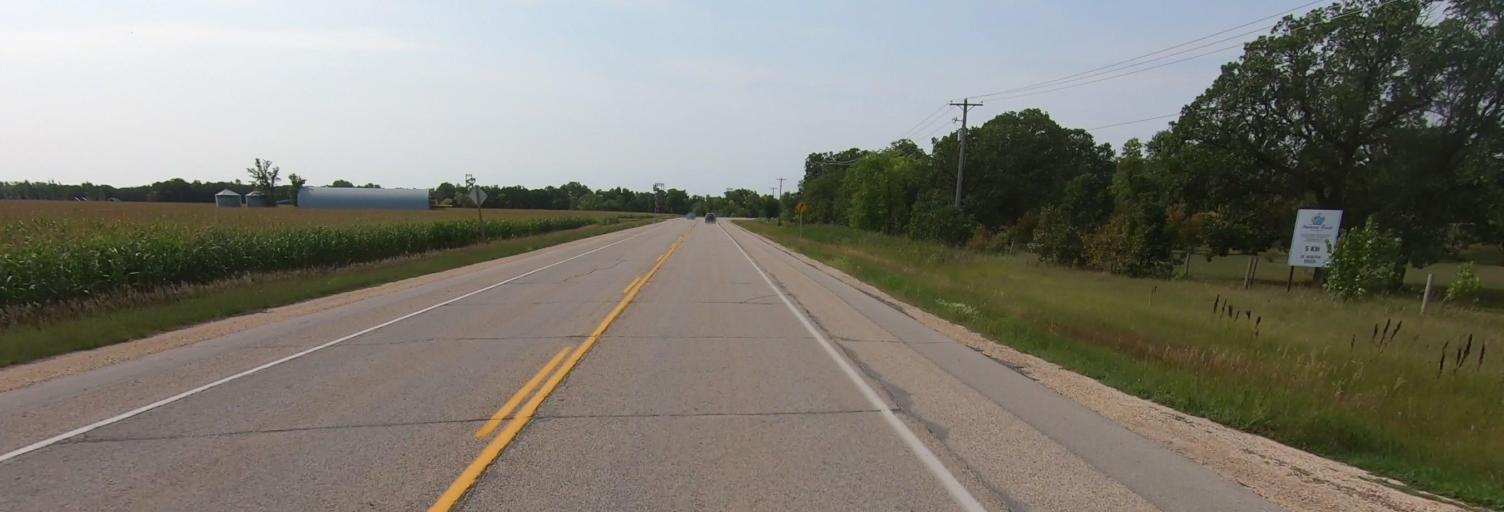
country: CA
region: Manitoba
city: Niverville
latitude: 49.7033
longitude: -97.0924
